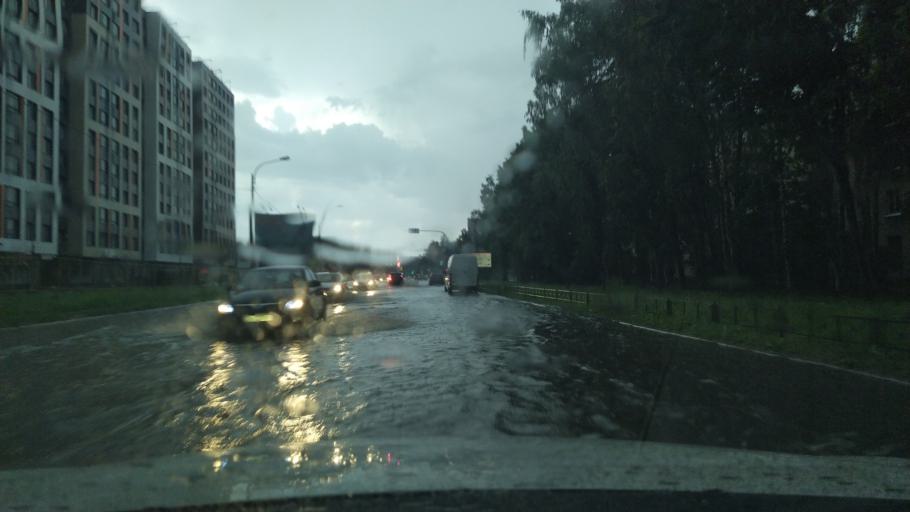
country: RU
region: Leningrad
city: Sampsonievskiy
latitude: 59.9829
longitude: 30.3533
